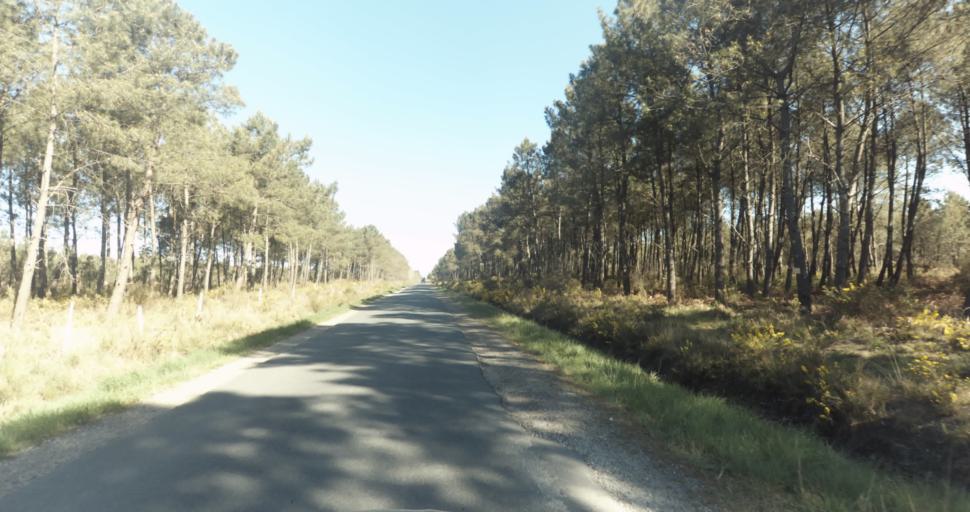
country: FR
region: Aquitaine
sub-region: Departement de la Gironde
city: Marcheprime
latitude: 44.7579
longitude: -0.8513
